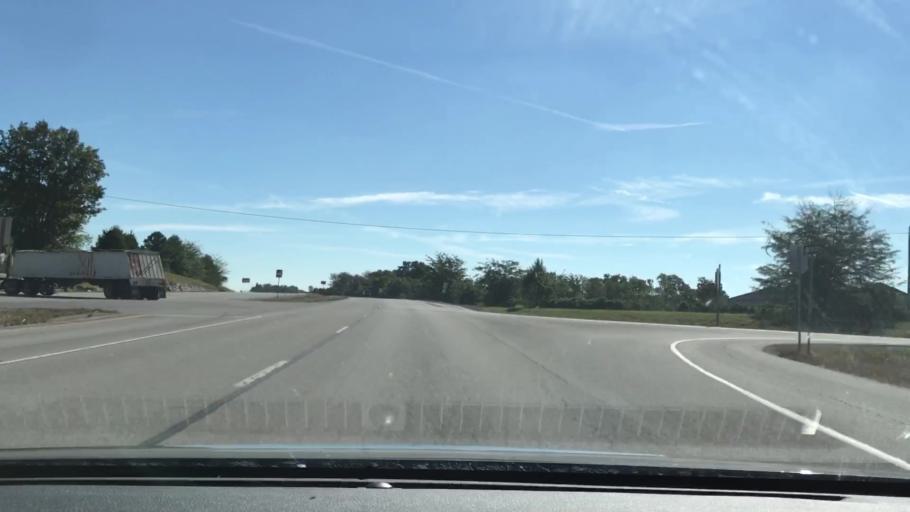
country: US
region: Kentucky
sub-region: Todd County
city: Elkton
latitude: 36.8272
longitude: -87.2212
